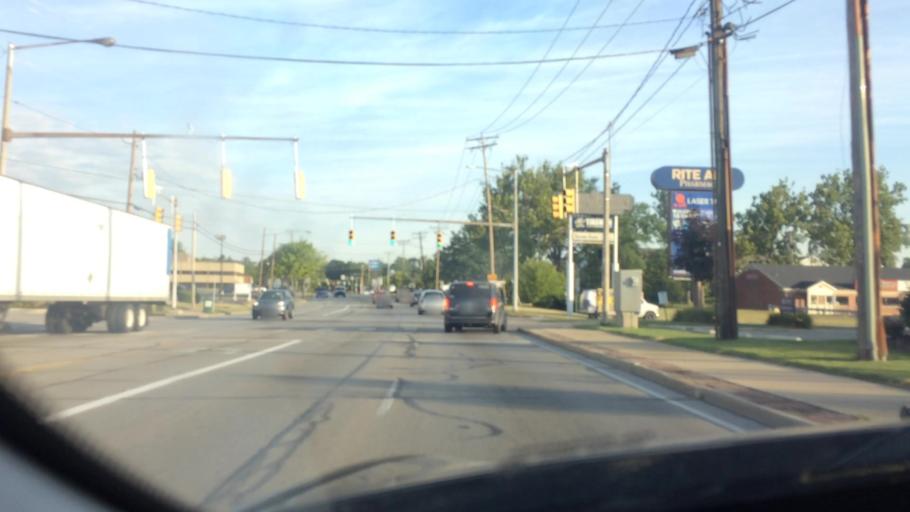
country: US
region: Ohio
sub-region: Lucas County
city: Sylvania
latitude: 41.7120
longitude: -83.6811
